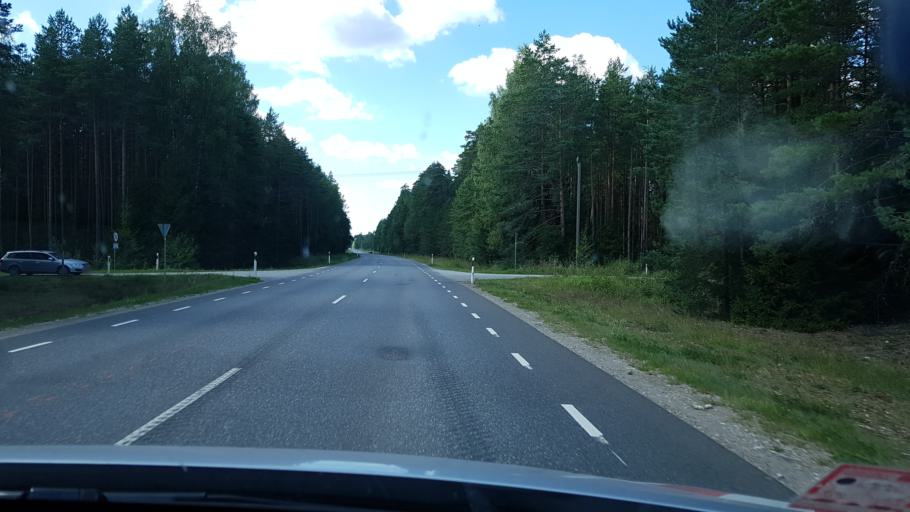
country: EE
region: Harju
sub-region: Kuusalu vald
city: Kuusalu
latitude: 59.3811
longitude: 25.4788
